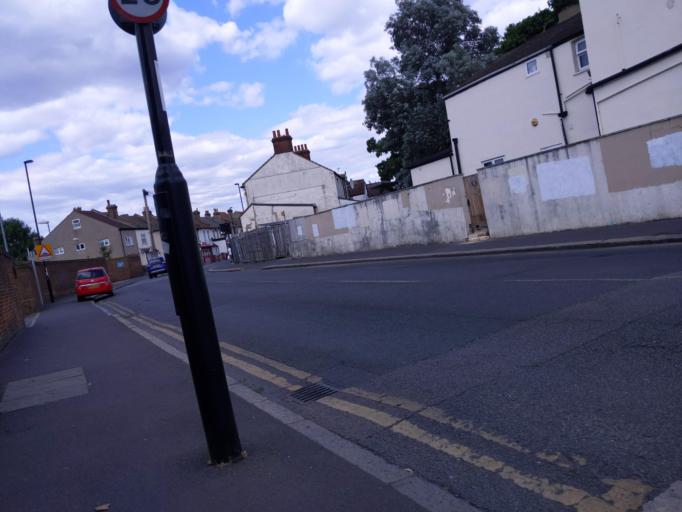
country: GB
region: England
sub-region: Greater London
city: Croydon
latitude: 51.3888
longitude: -0.1072
